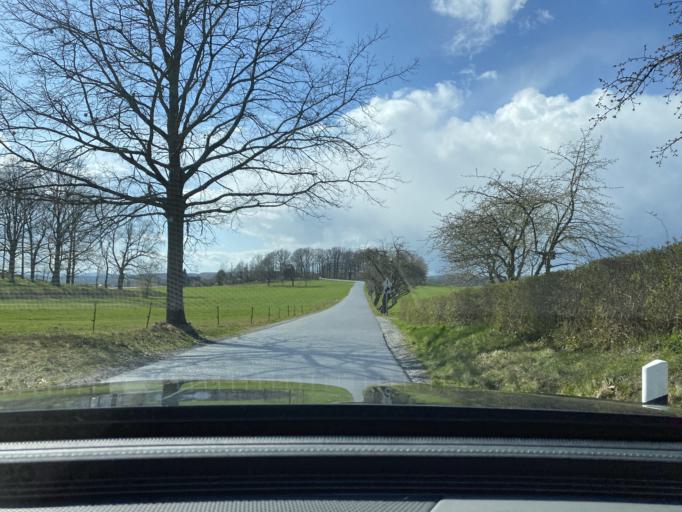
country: DE
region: Saxony
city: Radibor
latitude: 51.2484
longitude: 14.3657
